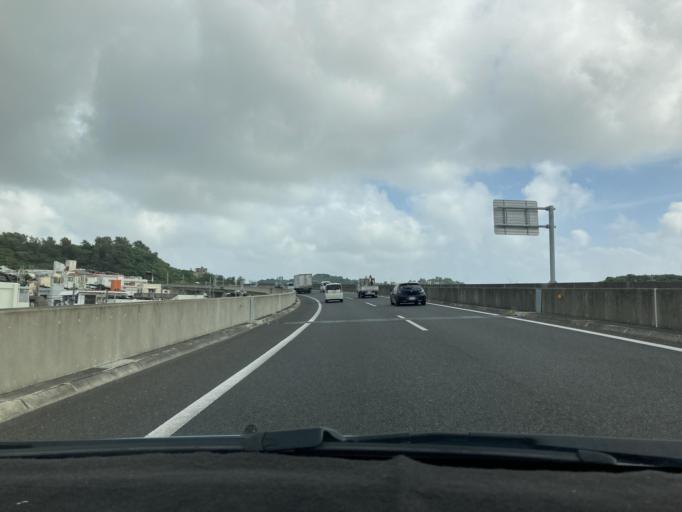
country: JP
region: Okinawa
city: Tomigusuku
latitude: 26.1731
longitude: 127.6761
